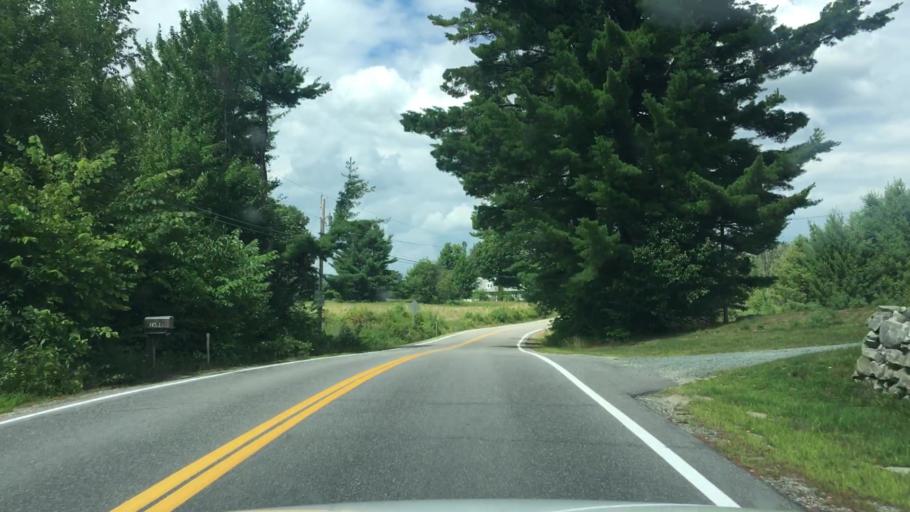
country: US
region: New Hampshire
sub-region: Coos County
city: Whitefield
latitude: 44.3078
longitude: -71.6590
